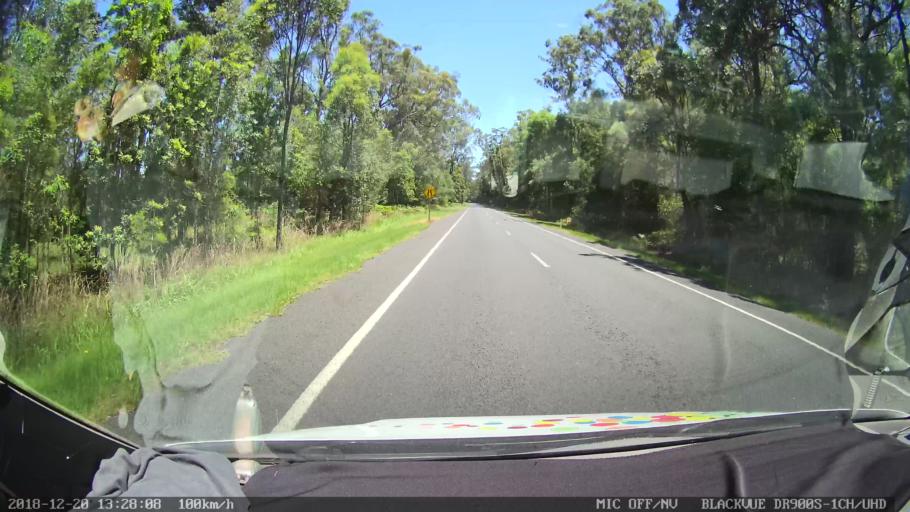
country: AU
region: New South Wales
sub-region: Clarence Valley
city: Gordon
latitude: -29.1702
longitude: 152.9918
